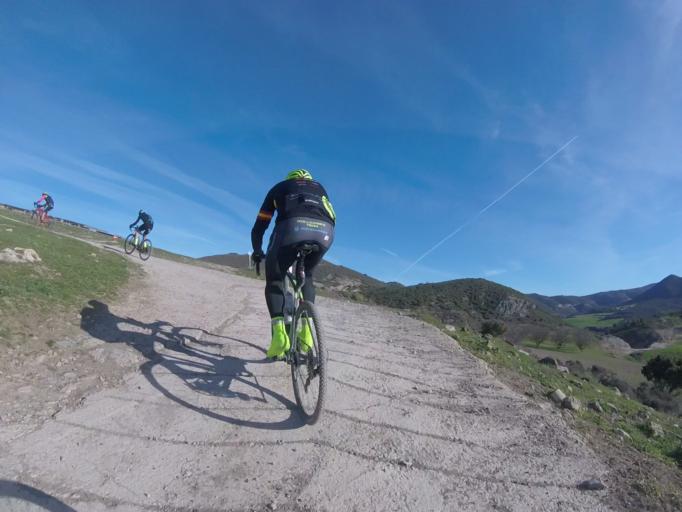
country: ES
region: Navarre
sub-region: Provincia de Navarra
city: Yerri
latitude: 42.6955
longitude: -1.9569
